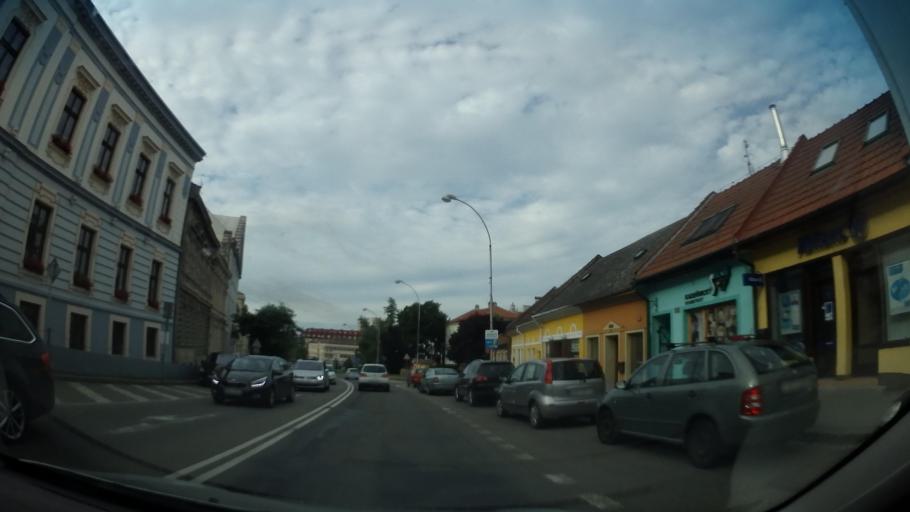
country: CZ
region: Zlin
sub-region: Okres Kromeriz
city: Kromeriz
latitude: 49.2968
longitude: 17.3977
